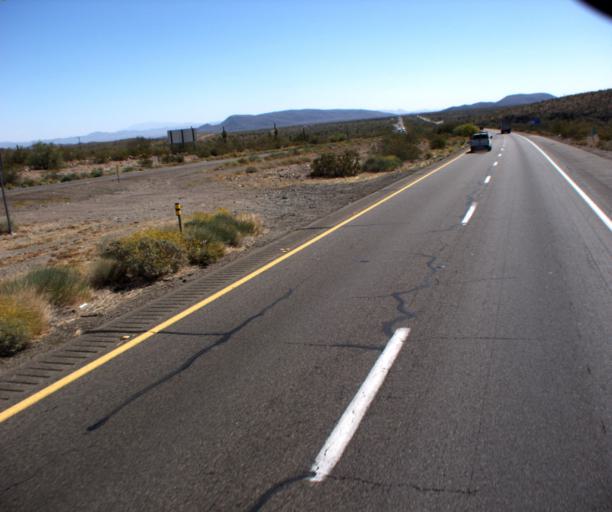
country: US
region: Arizona
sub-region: La Paz County
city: Quartzsite
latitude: 33.6645
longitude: -114.0316
